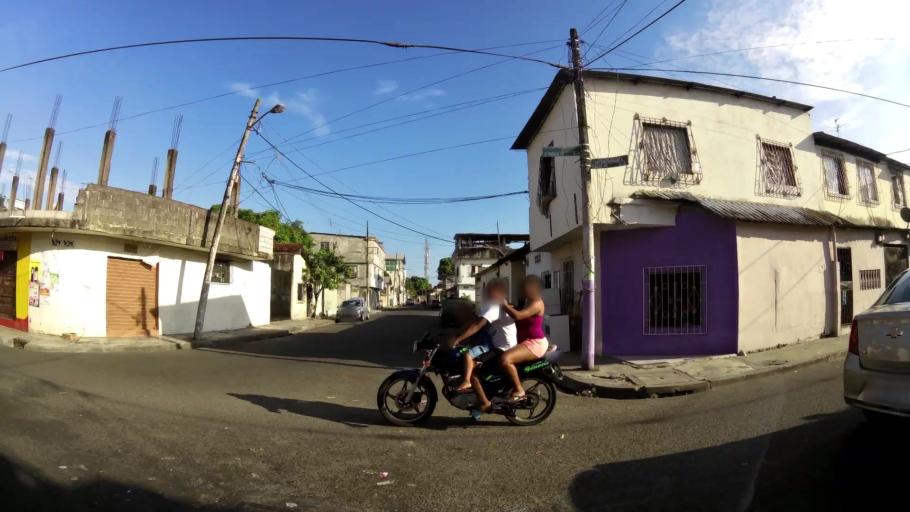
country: EC
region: Guayas
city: Guayaquil
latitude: -2.2248
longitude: -79.9081
